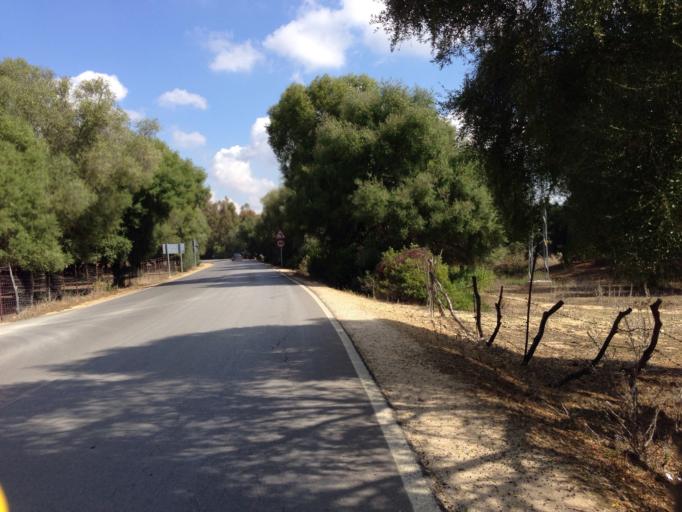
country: ES
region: Andalusia
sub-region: Provincia de Cadiz
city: Vejer de la Frontera
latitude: 36.2092
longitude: -6.0337
